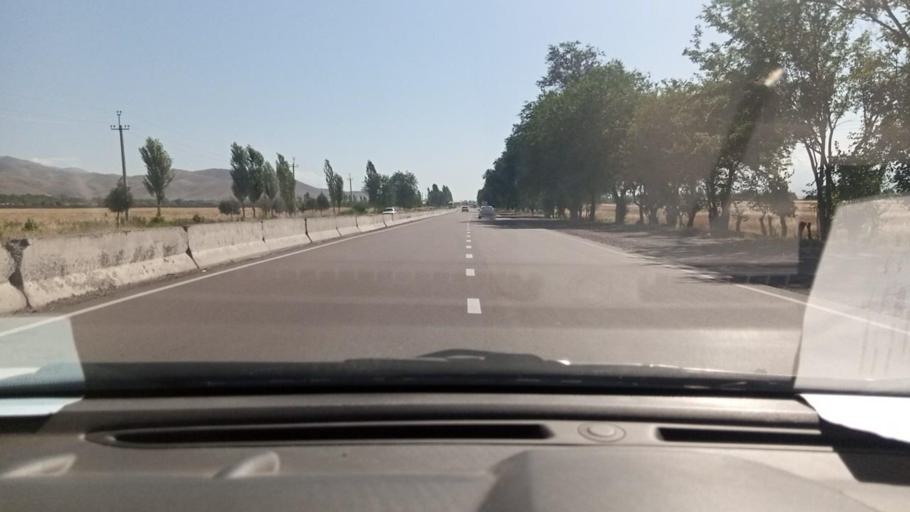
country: UZ
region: Toshkent
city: Ohangaron
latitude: 40.9255
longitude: 69.8460
